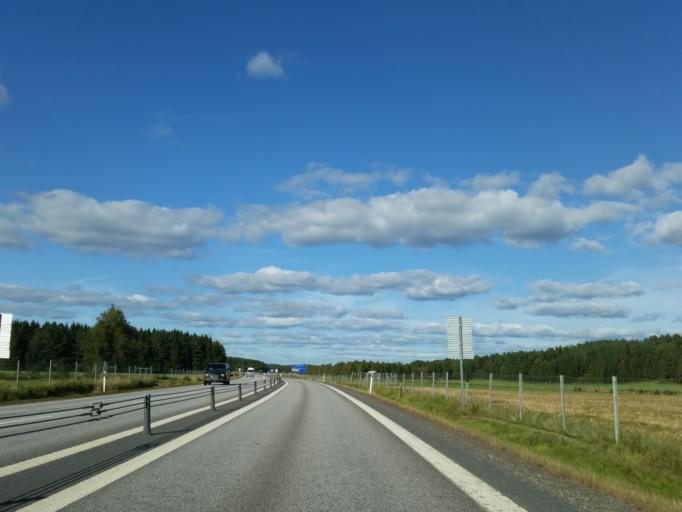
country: SE
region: Vaesterbotten
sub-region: Robertsfors Kommun
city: Robertsfors
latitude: 64.1329
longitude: 20.8918
